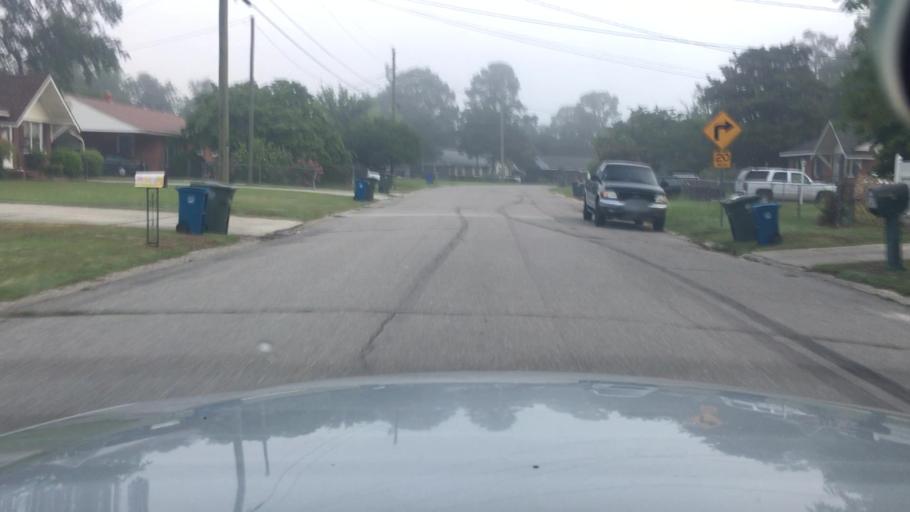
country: US
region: North Carolina
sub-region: Cumberland County
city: Hope Mills
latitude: 35.0208
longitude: -78.9449
